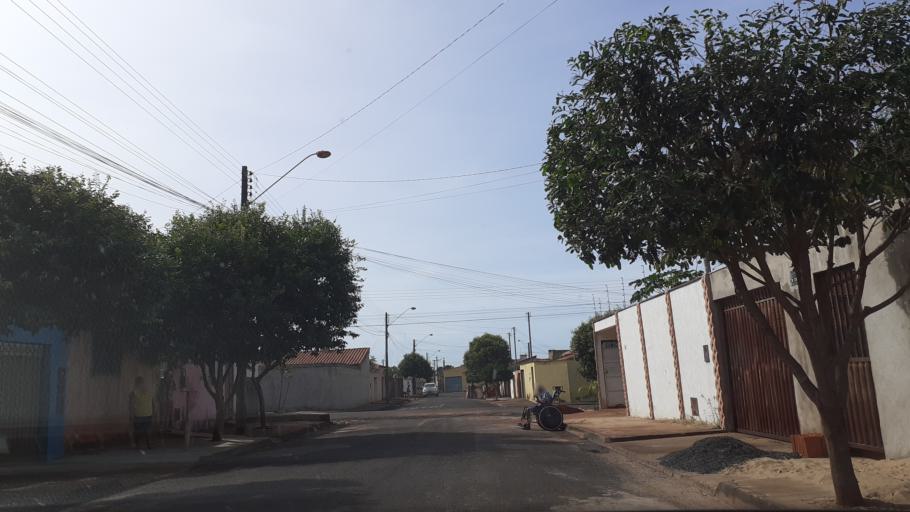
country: BR
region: Goias
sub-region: Itumbiara
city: Itumbiara
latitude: -18.4241
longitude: -49.2437
